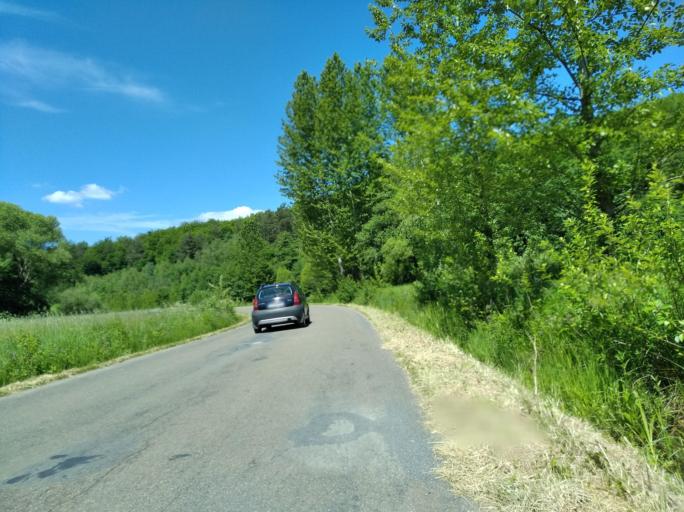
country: PL
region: Subcarpathian Voivodeship
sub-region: Powiat krosnienski
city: Chorkowka
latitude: 49.6366
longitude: 21.6032
